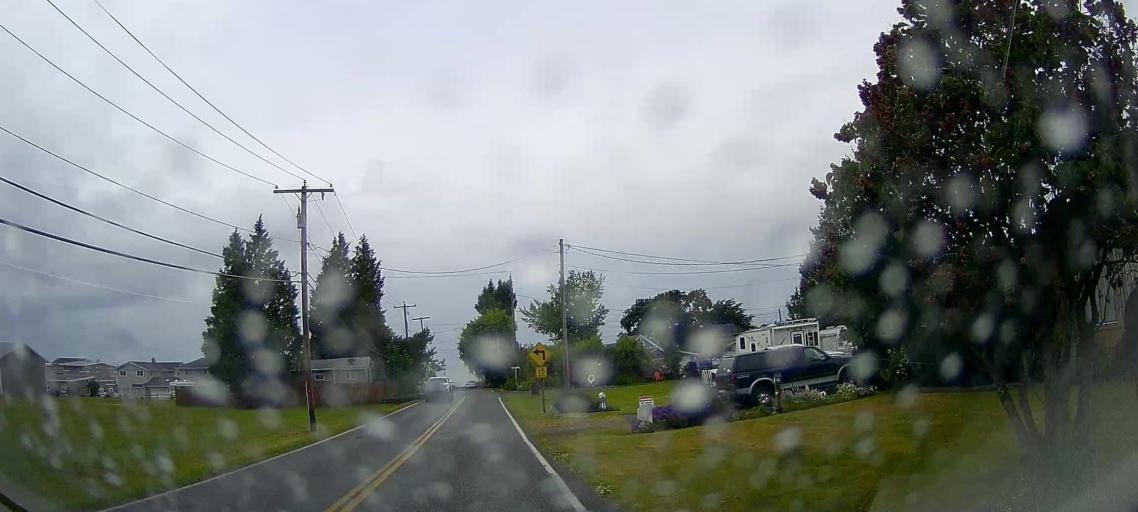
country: US
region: Washington
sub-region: Whatcom County
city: Birch Bay
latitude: 48.8161
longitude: -122.7073
